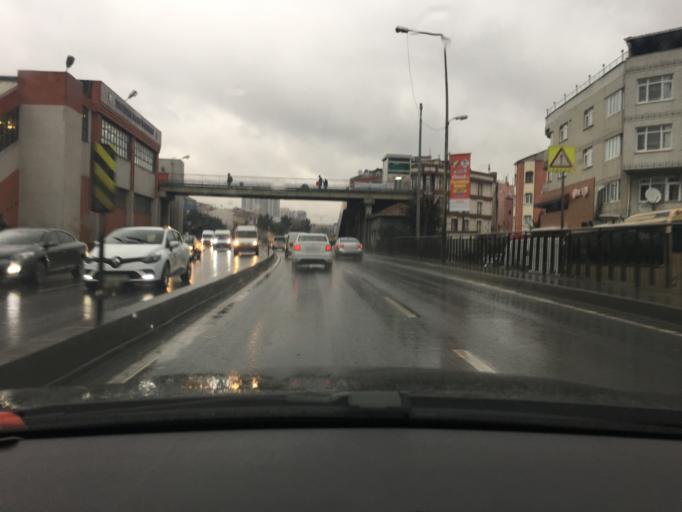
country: TR
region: Istanbul
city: merter keresteciler
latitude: 41.0302
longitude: 28.8984
